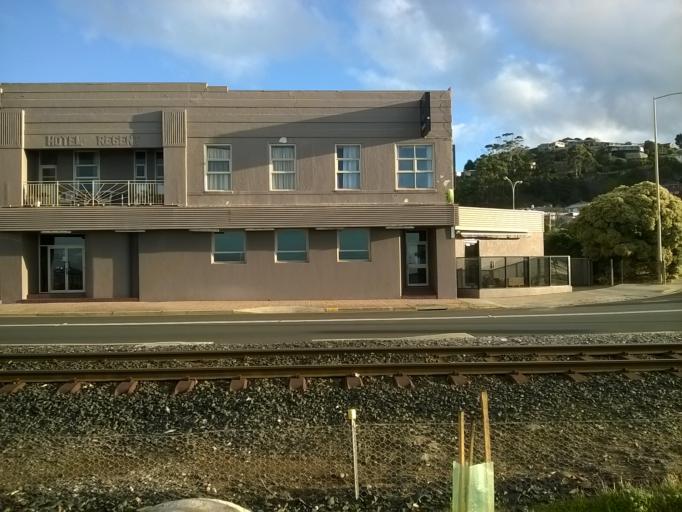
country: AU
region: Tasmania
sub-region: Burnie
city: Burnie
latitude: -41.0482
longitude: 145.9028
